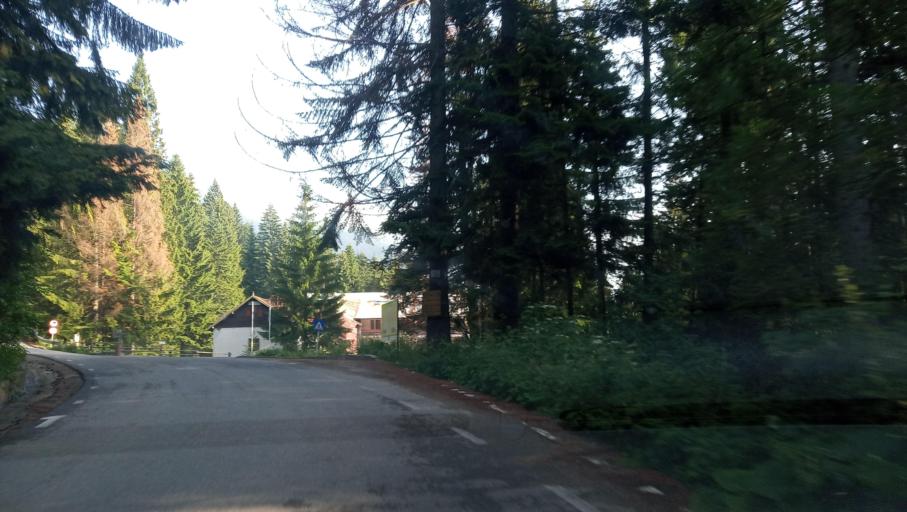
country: RO
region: Prahova
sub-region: Oras Sinaia
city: Sinaia
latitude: 45.3200
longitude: 25.5145
